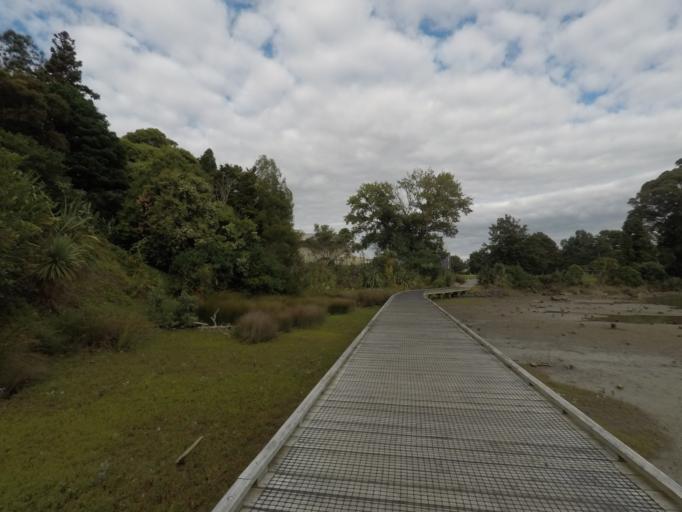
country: NZ
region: Auckland
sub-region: Auckland
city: Papakura
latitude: -37.0646
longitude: 174.9336
